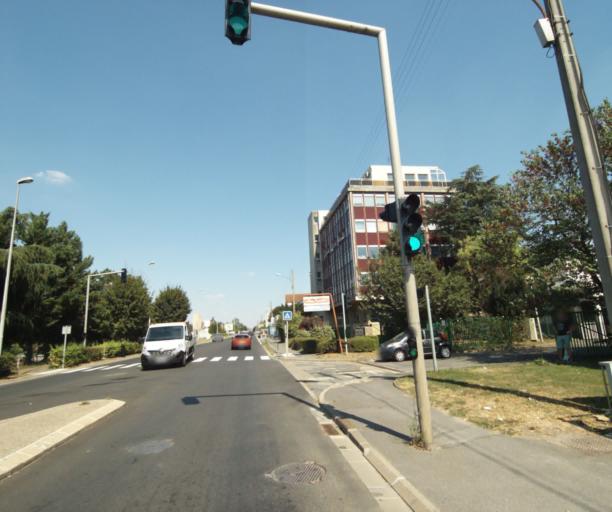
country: FR
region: Ile-de-France
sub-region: Departement de Seine-et-Marne
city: Saint-Thibault-des-Vignes
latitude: 48.8731
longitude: 2.6878
